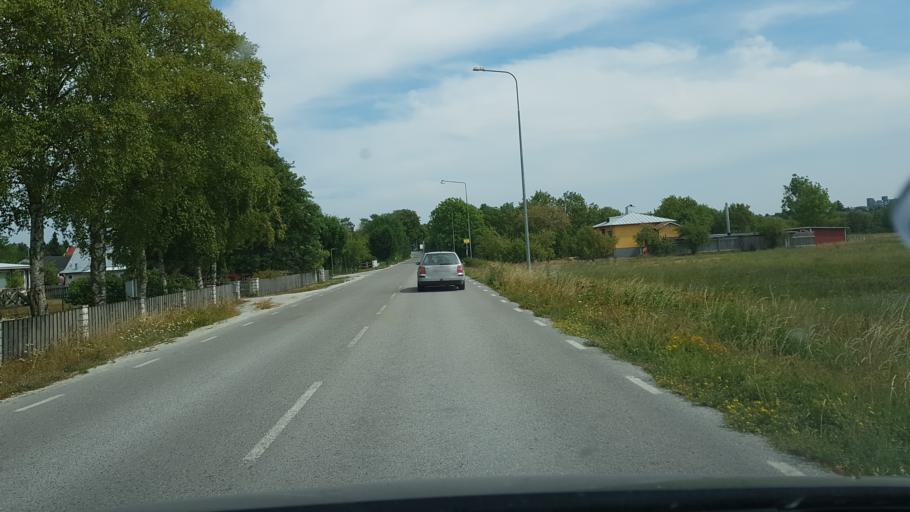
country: SE
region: Gotland
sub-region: Gotland
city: Slite
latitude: 57.7214
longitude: 18.7849
